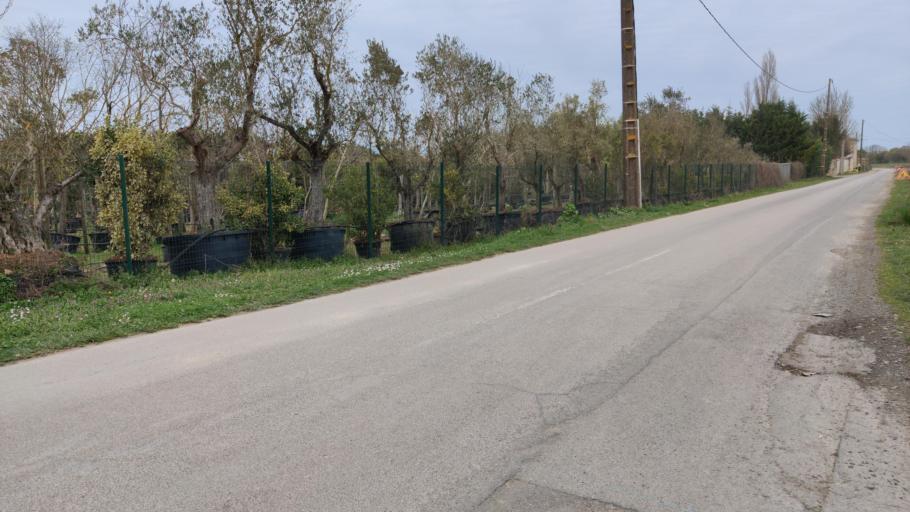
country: FR
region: Poitou-Charentes
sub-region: Departement de la Charente-Maritime
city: Salles-sur-Mer
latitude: 46.1236
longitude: -1.0468
